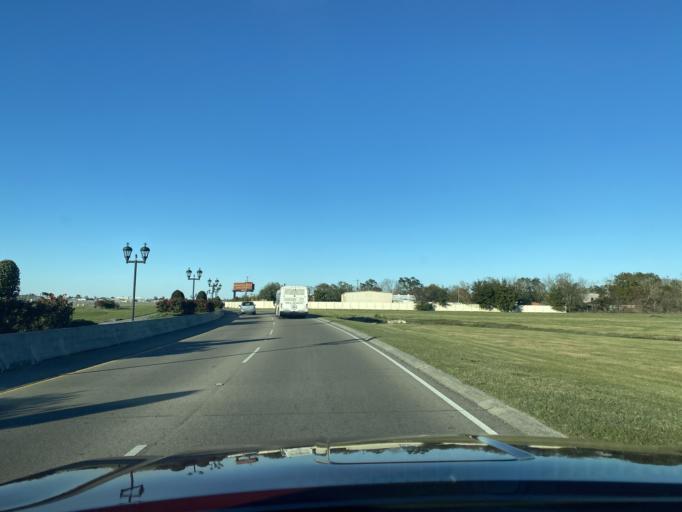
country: US
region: Louisiana
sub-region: Jefferson Parish
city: Kenner
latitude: 29.9886
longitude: -90.2479
